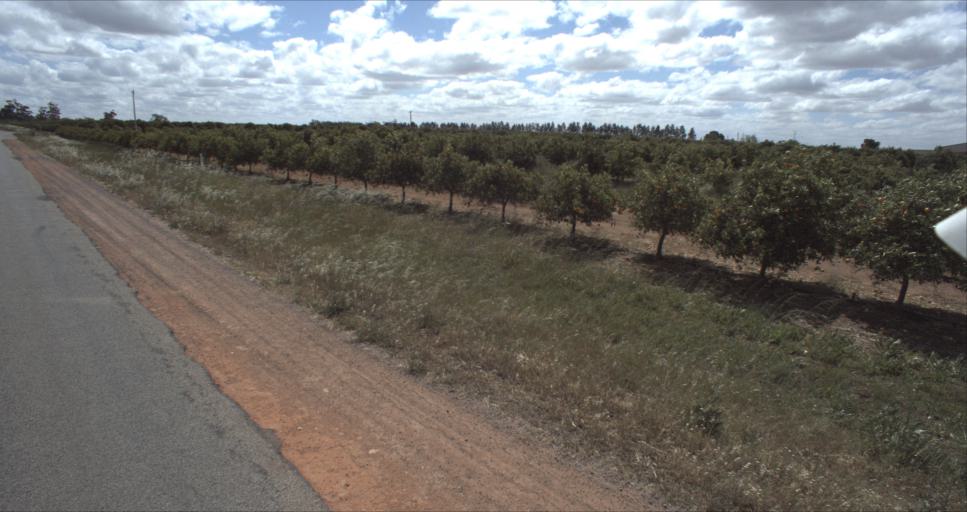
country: AU
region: New South Wales
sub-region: Leeton
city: Leeton
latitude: -34.5881
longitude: 146.3802
